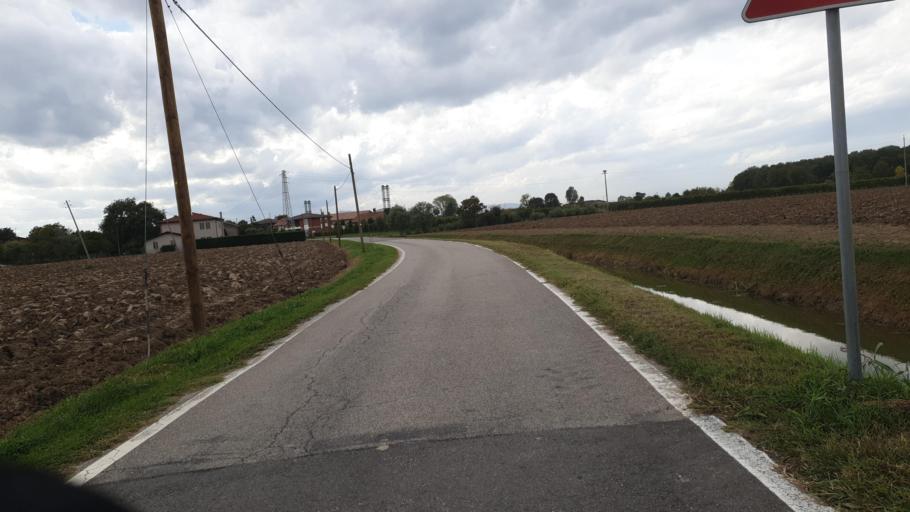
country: IT
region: Veneto
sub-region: Provincia di Padova
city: Bovolenta
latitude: 45.2907
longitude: 11.9353
